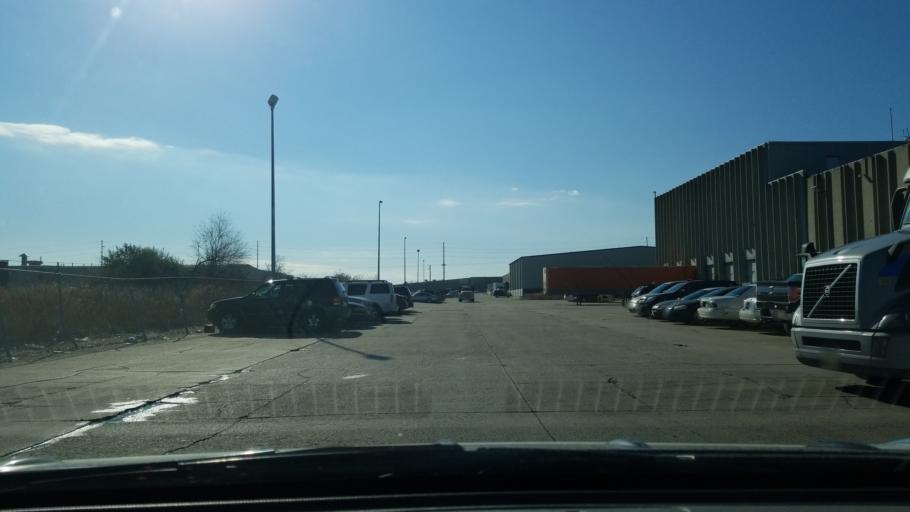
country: US
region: Nebraska
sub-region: Douglas County
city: Ralston
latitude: 41.2187
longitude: -96.0737
